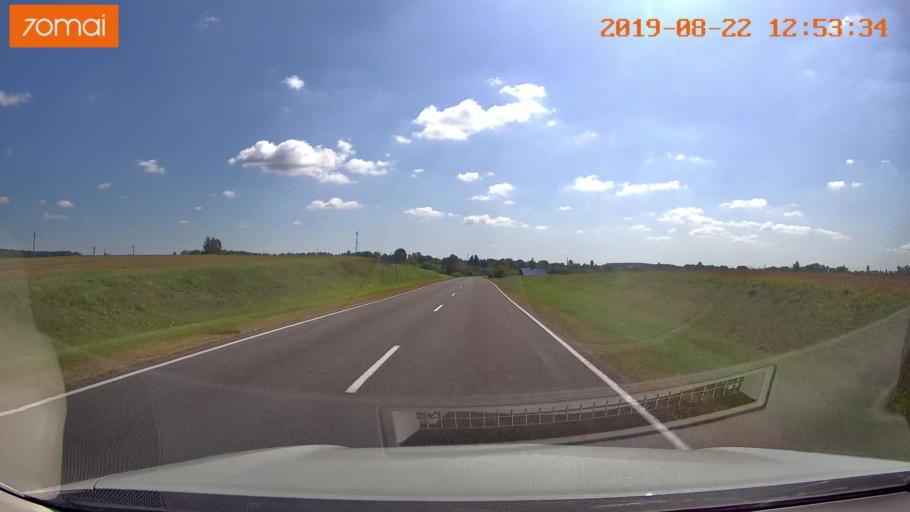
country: BY
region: Minsk
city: Prawdzinski
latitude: 53.4448
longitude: 27.6884
